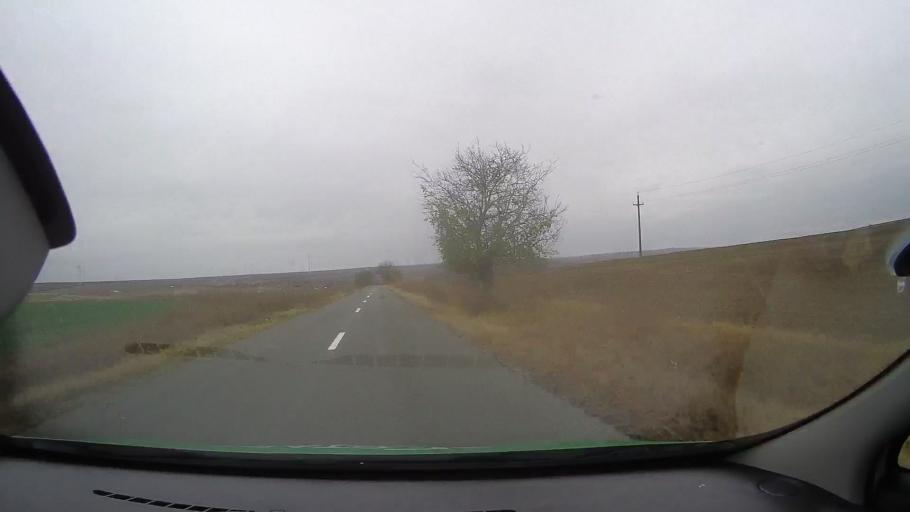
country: RO
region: Constanta
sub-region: Comuna Targusor
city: Targusor
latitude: 44.4836
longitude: 28.3693
